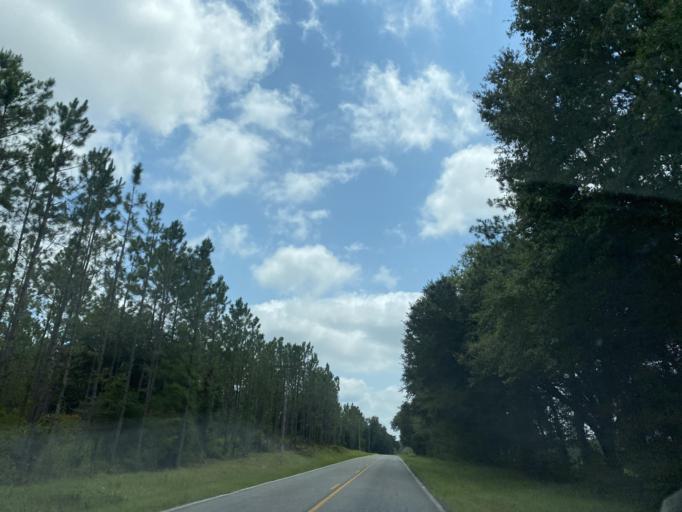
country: US
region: Georgia
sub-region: Wheeler County
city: Alamo
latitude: 32.1211
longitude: -82.7883
